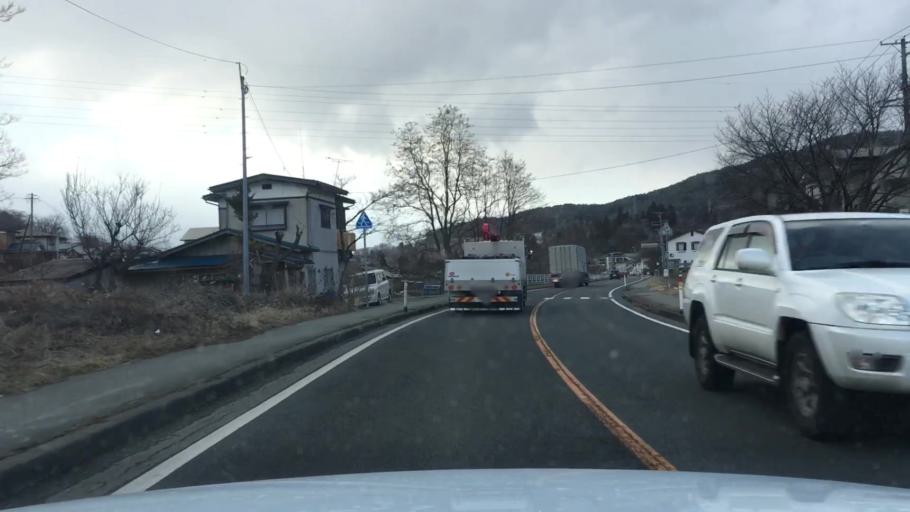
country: JP
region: Iwate
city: Morioka-shi
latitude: 39.6823
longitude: 141.1826
